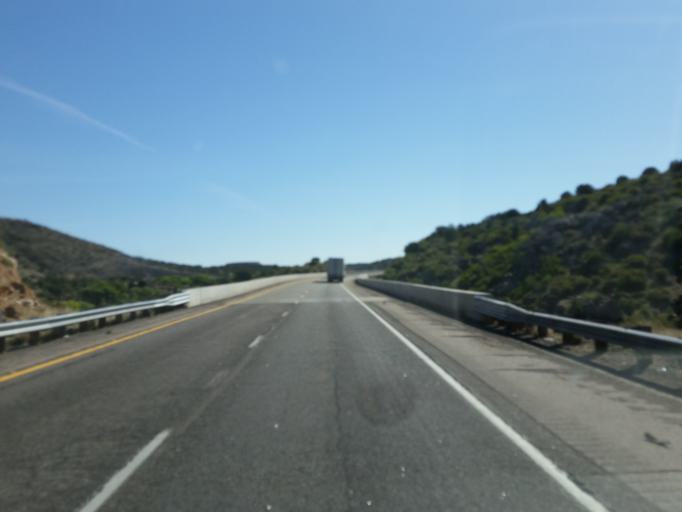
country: US
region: Arizona
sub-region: Mohave County
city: Peach Springs
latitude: 35.1785
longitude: -113.4733
